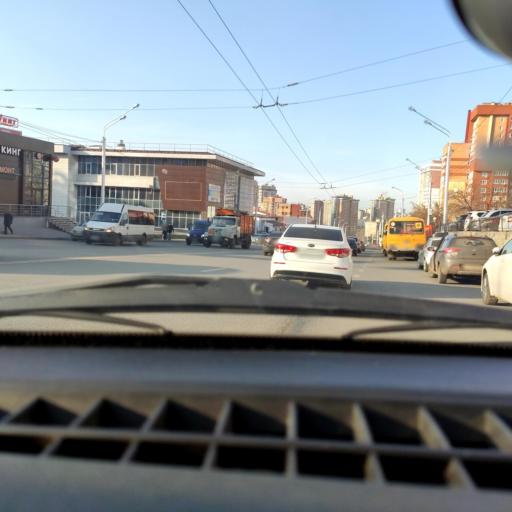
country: RU
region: Bashkortostan
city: Ufa
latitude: 54.7137
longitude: 55.9966
